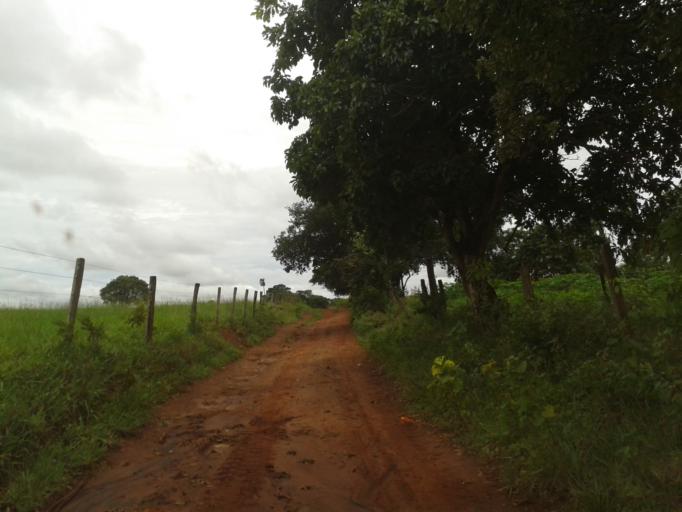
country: BR
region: Minas Gerais
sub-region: Capinopolis
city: Capinopolis
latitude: -18.7965
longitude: -49.7875
